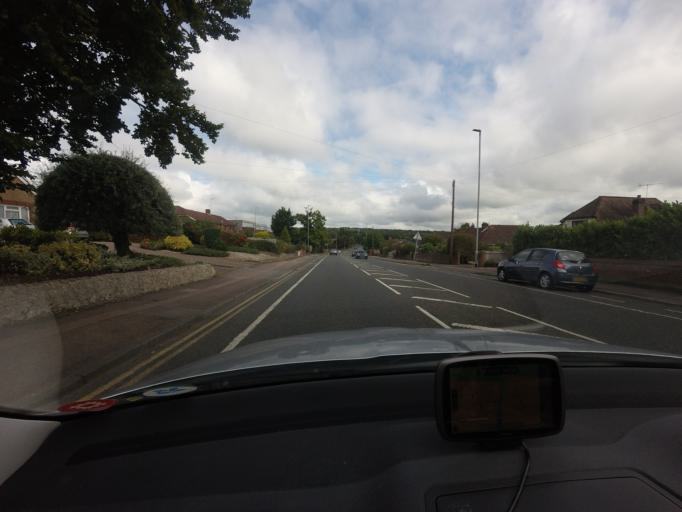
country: GB
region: England
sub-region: Kent
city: Tonbridge
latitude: 51.2149
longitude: 0.2810
